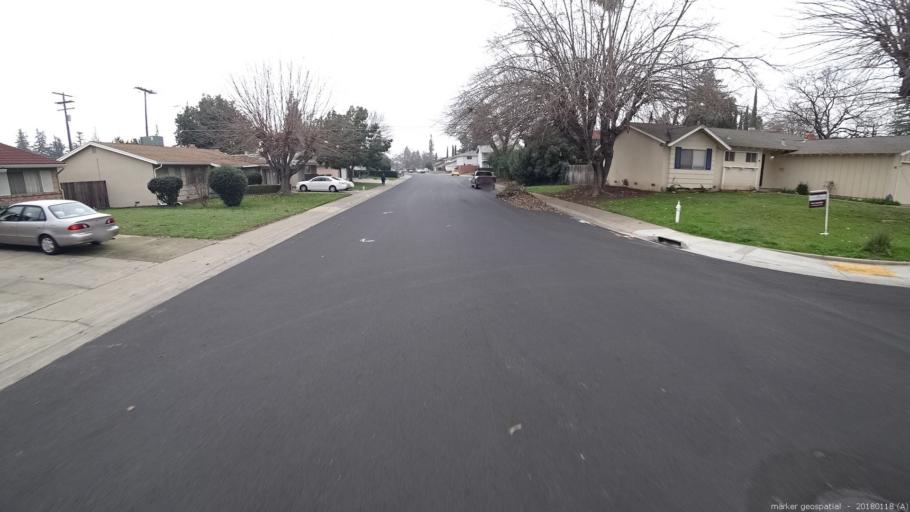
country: US
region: California
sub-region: Sacramento County
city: Rancho Cordova
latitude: 38.5915
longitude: -121.3171
